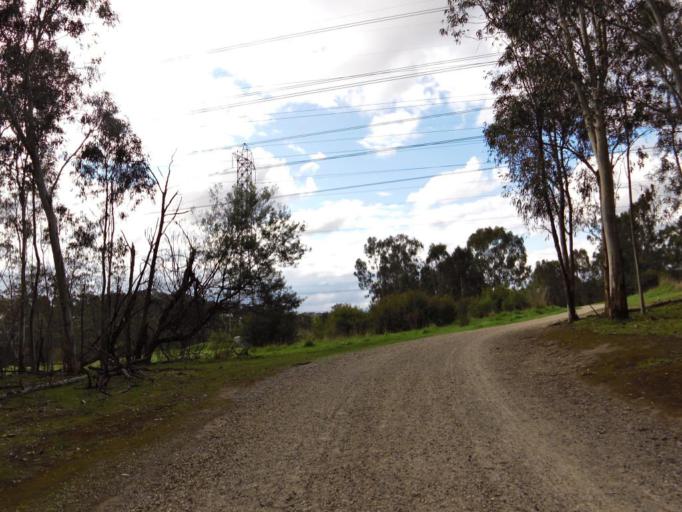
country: AU
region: Victoria
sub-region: Nillumbik
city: Eltham
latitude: -37.7417
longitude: 145.1404
